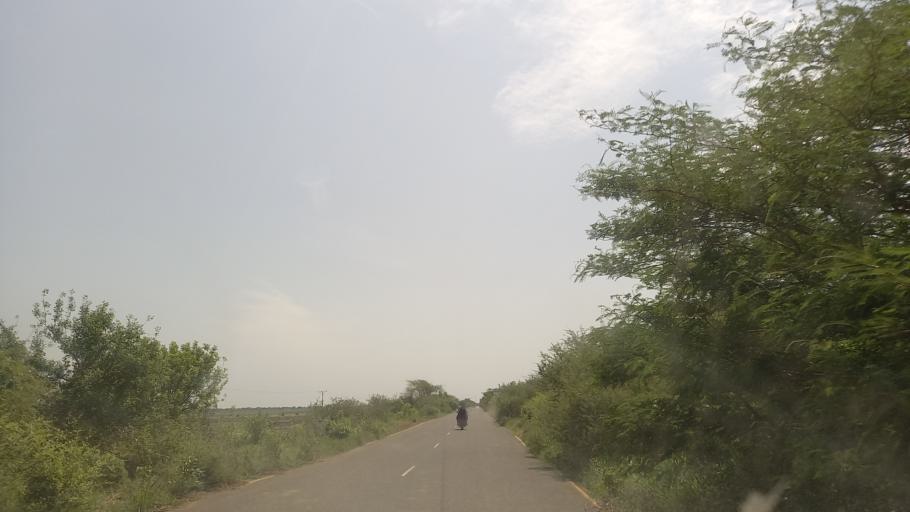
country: ET
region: Gambela
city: Gambela
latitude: 8.2846
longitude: 34.2128
